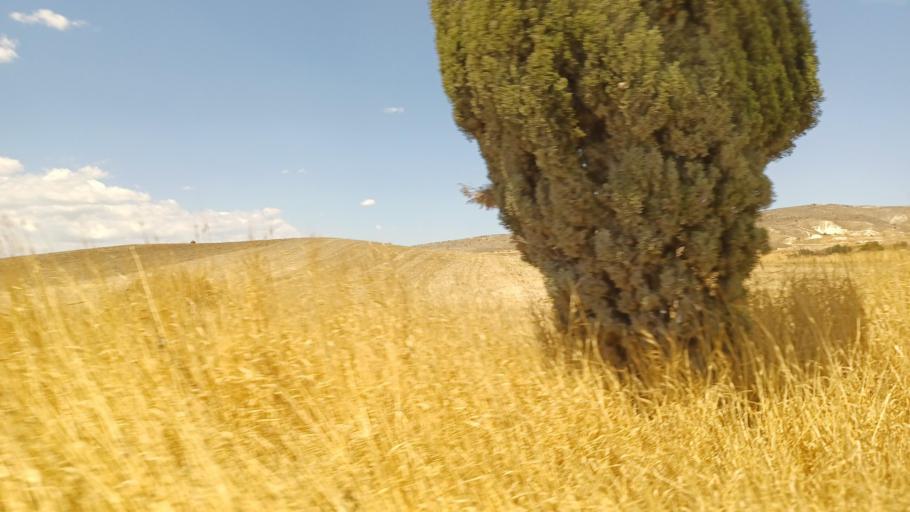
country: CY
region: Larnaka
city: Troulloi
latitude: 35.0419
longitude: 33.6169
